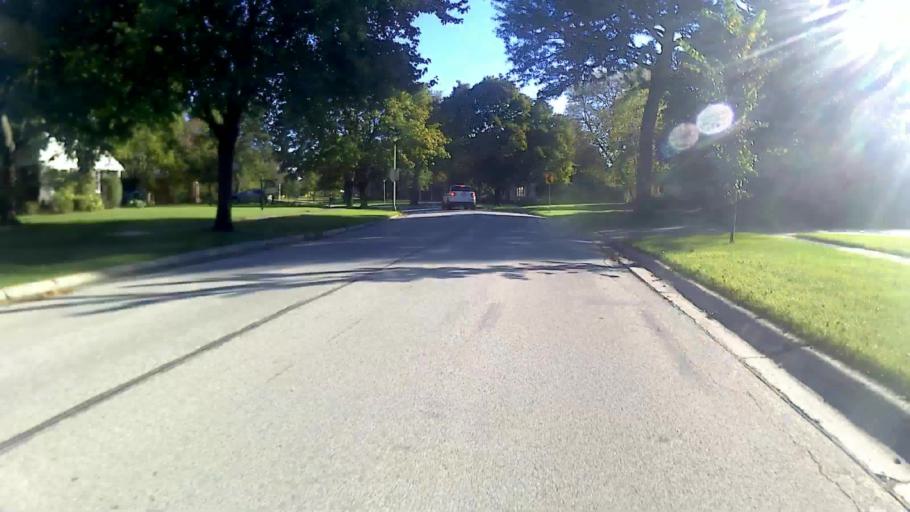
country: US
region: Illinois
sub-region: DuPage County
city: Wheaton
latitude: 41.8478
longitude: -88.1034
